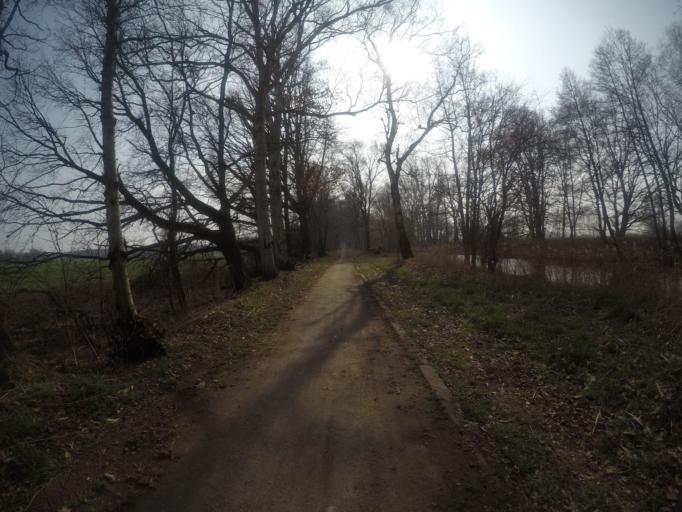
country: DE
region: Brandenburg
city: Mittenwalde
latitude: 52.2776
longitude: 13.5645
